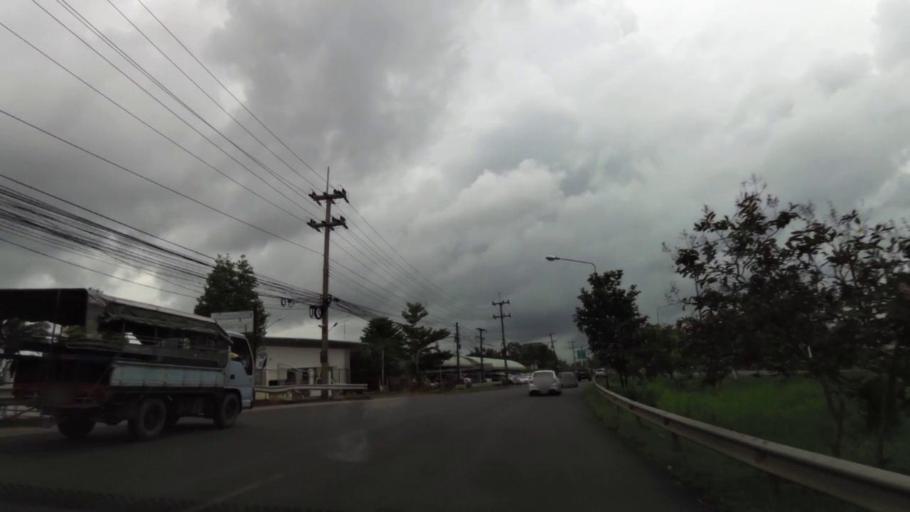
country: TH
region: Chanthaburi
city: Chanthaburi
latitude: 12.6090
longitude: 102.1341
